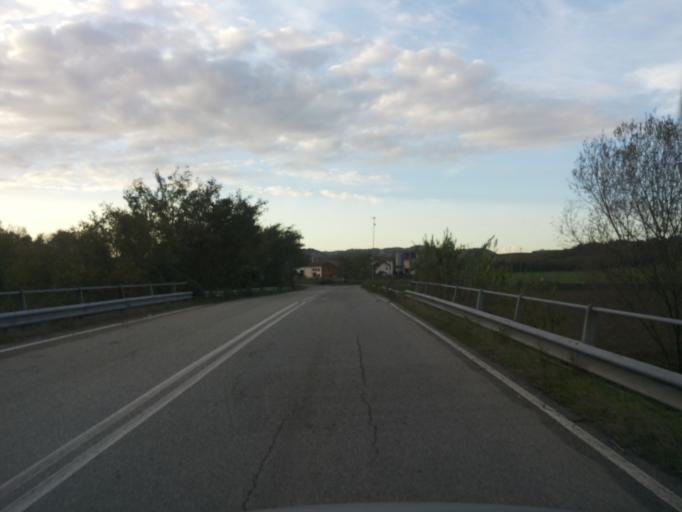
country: IT
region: Piedmont
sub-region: Provincia di Alessandria
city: Cereseto
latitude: 45.1131
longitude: 8.3237
